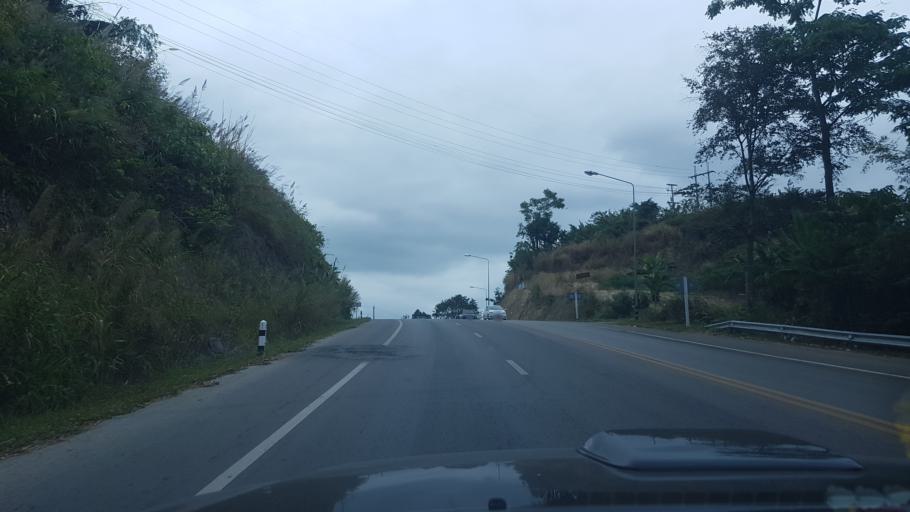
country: TH
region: Phetchabun
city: Khao Kho
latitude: 16.5564
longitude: 101.0263
